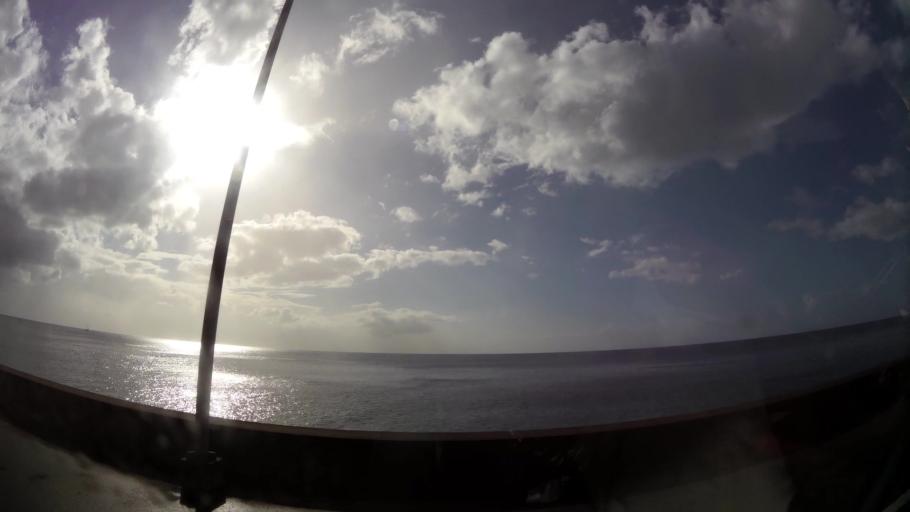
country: DM
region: Saint George
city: Roseau
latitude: 15.3251
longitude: -61.3955
